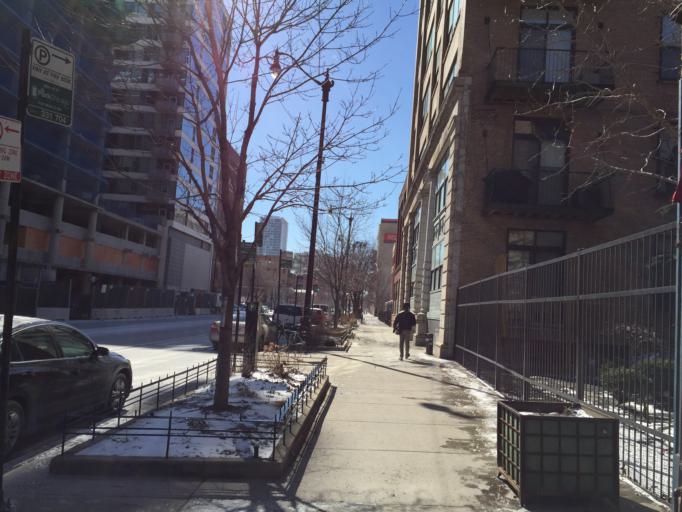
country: US
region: Illinois
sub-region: Cook County
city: Chicago
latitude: 41.8653
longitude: -87.6260
